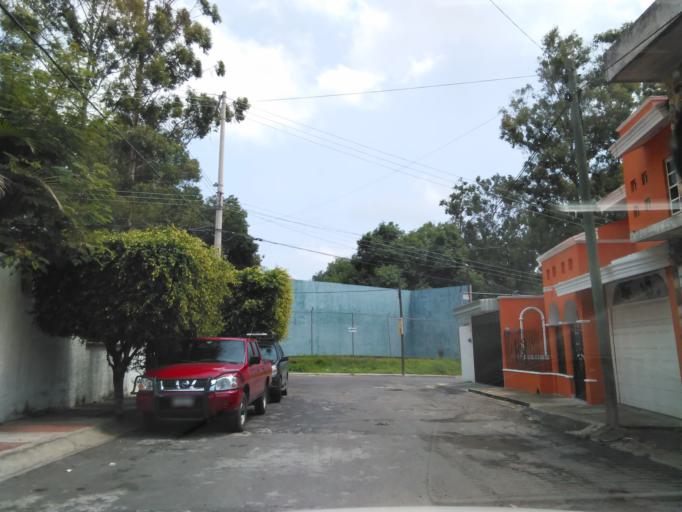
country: MX
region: Nayarit
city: Tepic
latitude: 21.5135
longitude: -104.9218
